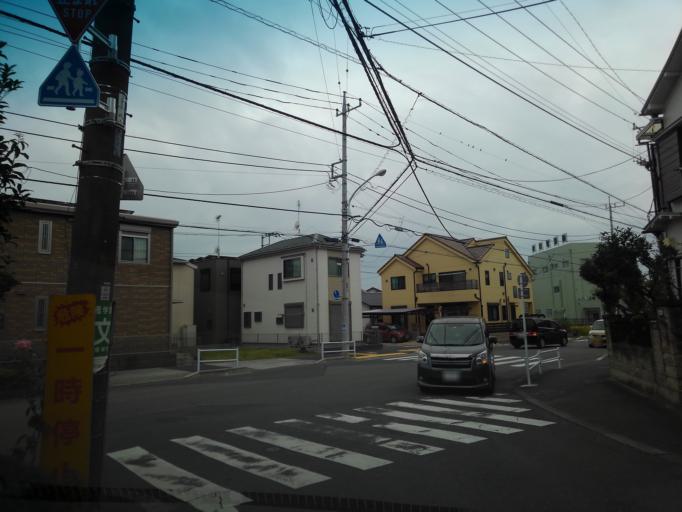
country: JP
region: Tokyo
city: Chofugaoka
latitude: 35.6432
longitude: 139.5197
